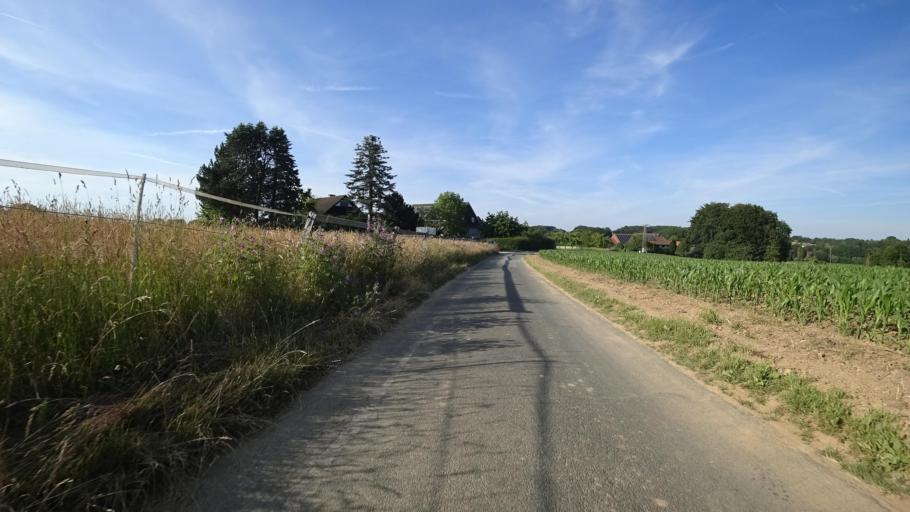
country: DE
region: Lower Saxony
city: Neuenkirchen
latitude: 52.1093
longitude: 8.4061
